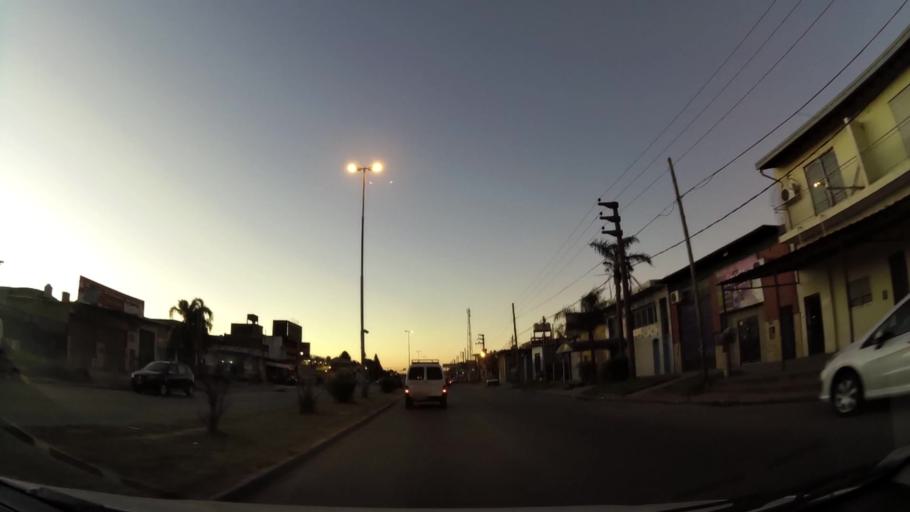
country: AR
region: Buenos Aires
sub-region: Partido de Moron
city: Moron
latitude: -34.7109
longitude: -58.6082
